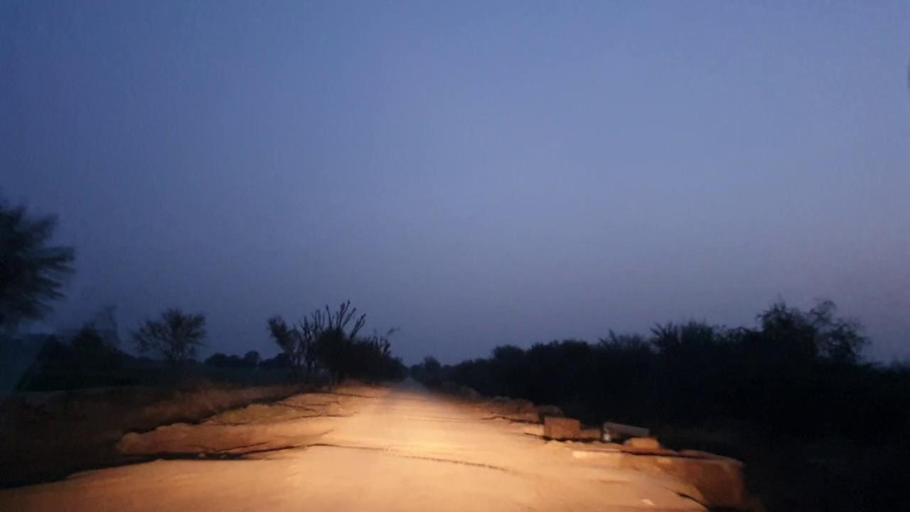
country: PK
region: Sindh
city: Tando Ghulam Ali
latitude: 25.0876
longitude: 68.9193
